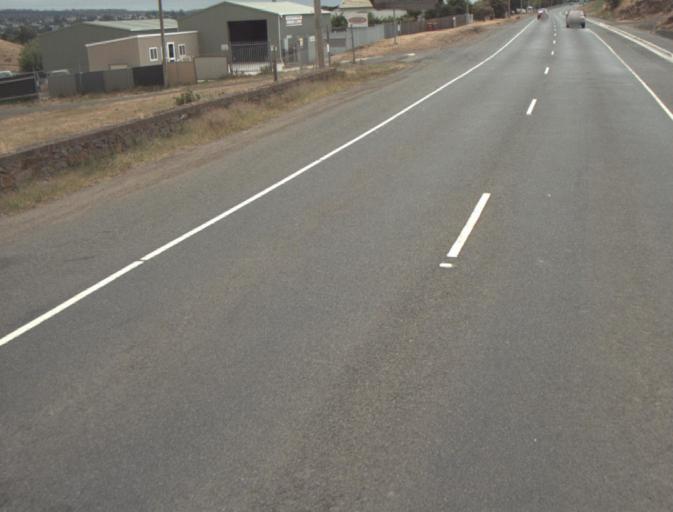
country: AU
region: Tasmania
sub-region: Launceston
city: Newstead
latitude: -41.4481
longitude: 147.1875
